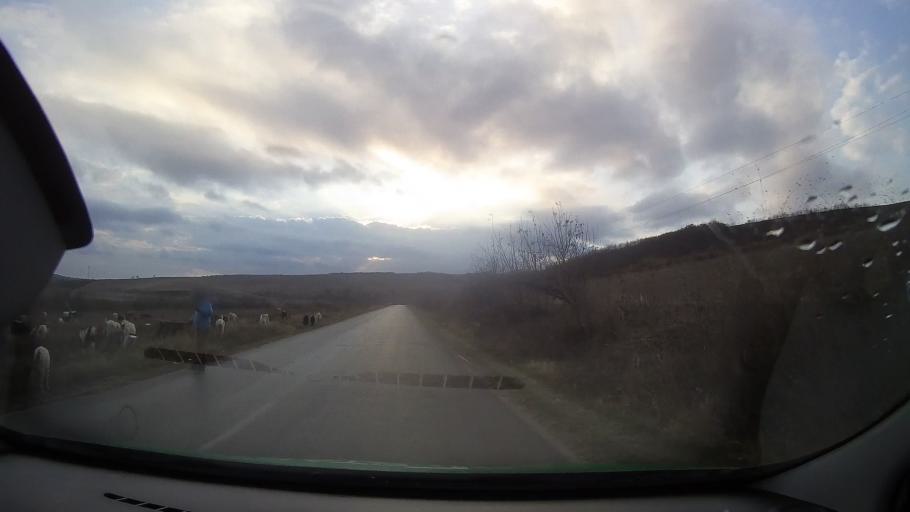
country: RO
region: Constanta
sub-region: Comuna Dobromir
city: Dobromir
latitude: 44.0319
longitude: 27.8342
